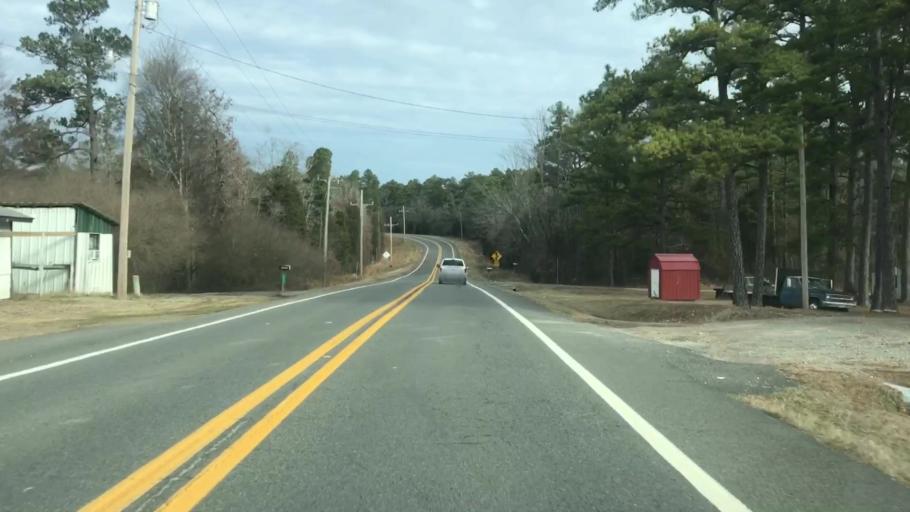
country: US
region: Arkansas
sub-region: Montgomery County
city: Mount Ida
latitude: 34.5853
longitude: -93.6633
